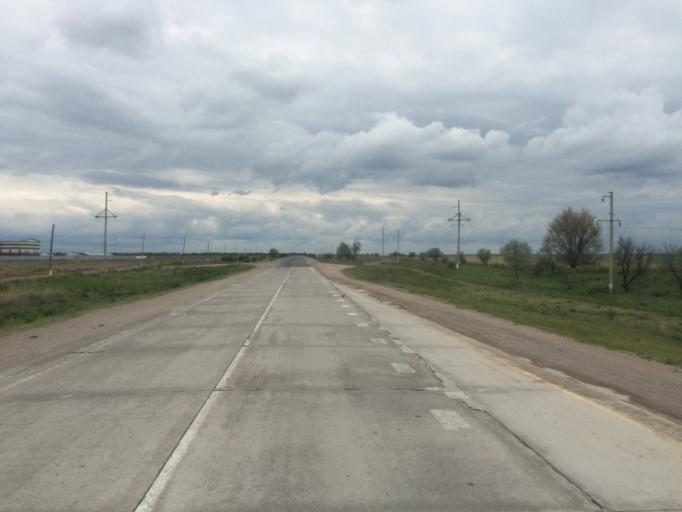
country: KG
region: Chuy
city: Sokuluk
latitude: 43.2698
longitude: 74.2438
